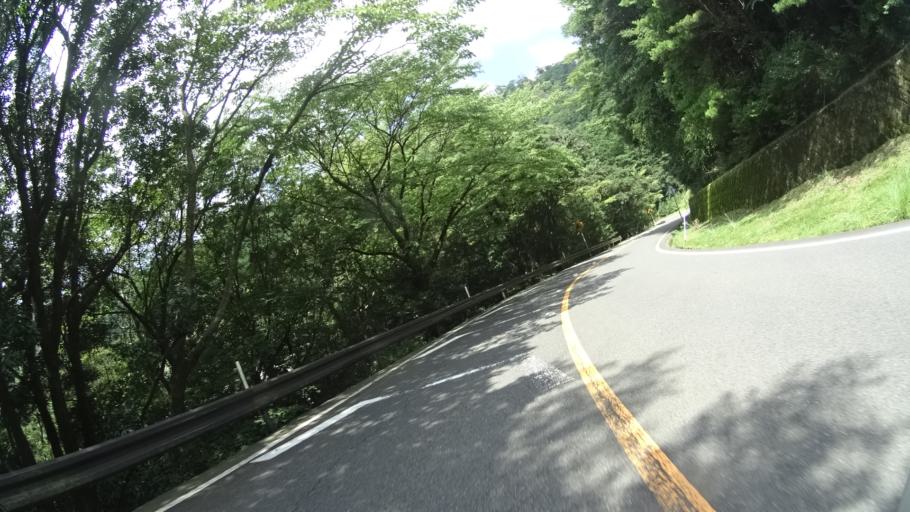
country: JP
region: Miyazaki
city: Kobayashi
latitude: 31.9035
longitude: 130.8460
